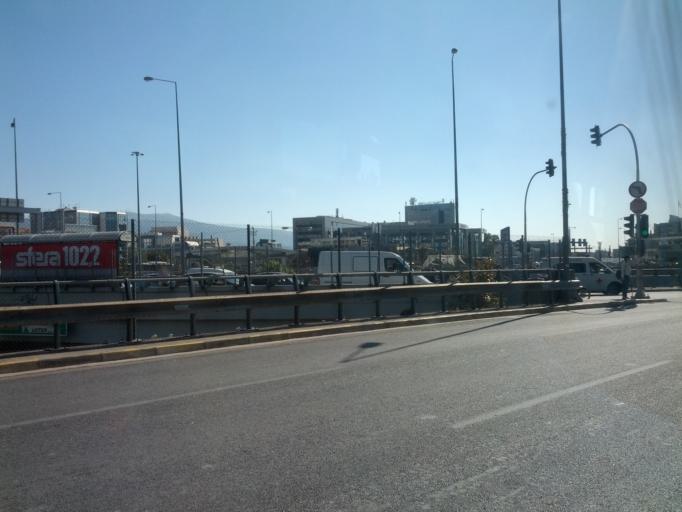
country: GR
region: Attica
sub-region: Nomarchia Athinas
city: Marousi
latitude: 38.0431
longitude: 23.8039
